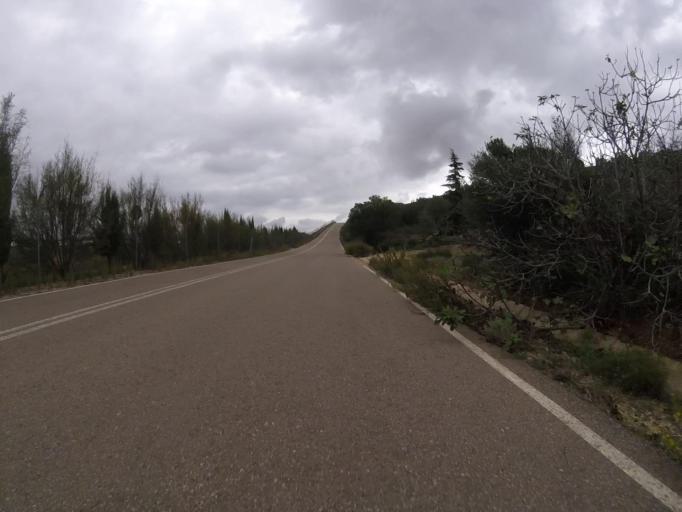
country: ES
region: Valencia
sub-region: Provincia de Castello
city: Cabanes
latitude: 40.1861
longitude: 0.0469
